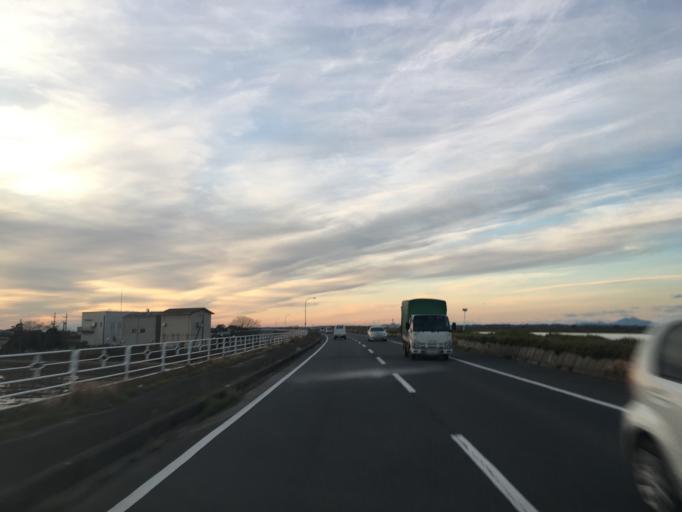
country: JP
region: Chiba
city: Katori-shi
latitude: 35.9142
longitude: 140.4690
